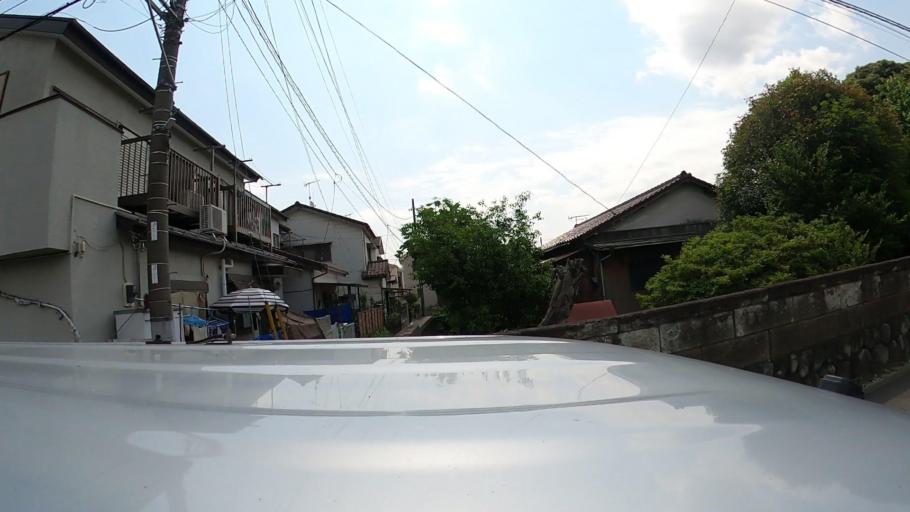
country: JP
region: Kanagawa
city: Chigasaki
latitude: 35.3643
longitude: 139.3883
